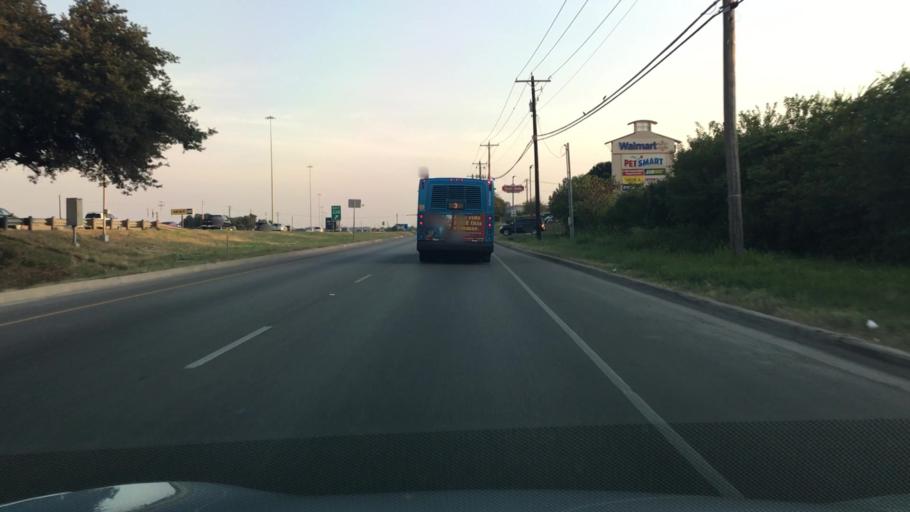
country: US
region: Texas
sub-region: Travis County
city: Onion Creek
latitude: 30.1644
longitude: -97.7882
